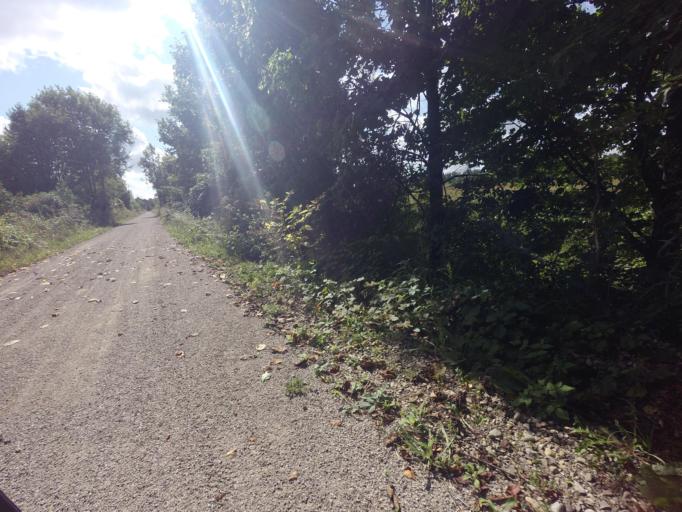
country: CA
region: Ontario
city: Huron East
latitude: 43.7225
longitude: -81.4024
